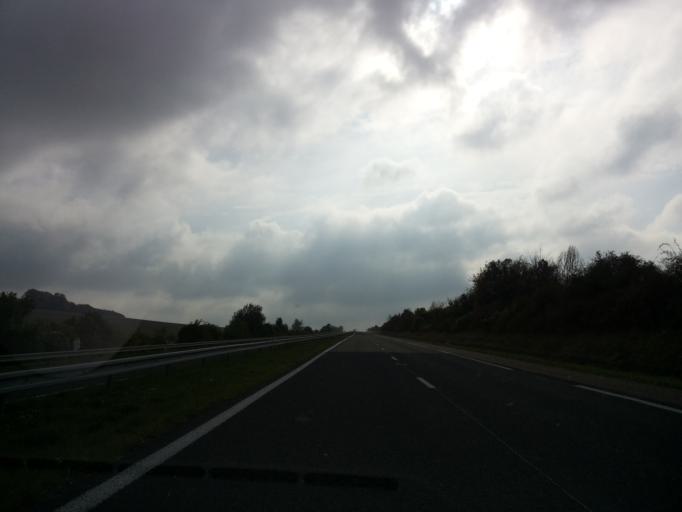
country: FR
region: Lorraine
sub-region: Departement de la Moselle
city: Solgne
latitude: 48.9426
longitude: 6.3222
